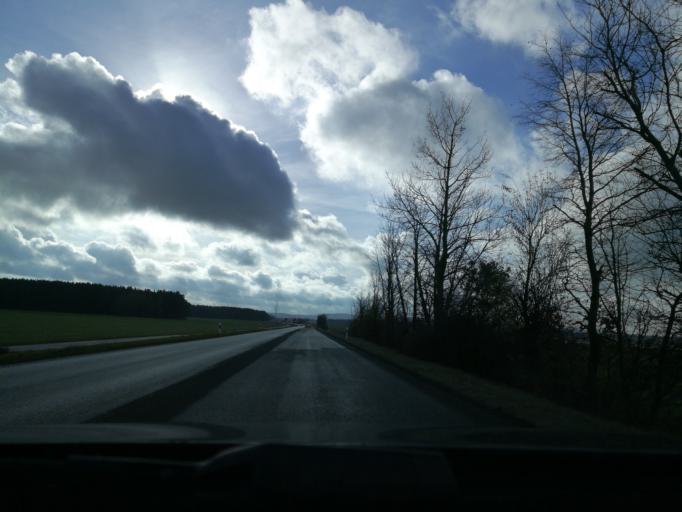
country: DE
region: Bavaria
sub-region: Regierungsbezirk Mittelfranken
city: Abenberg
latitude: 49.2525
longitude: 10.9009
